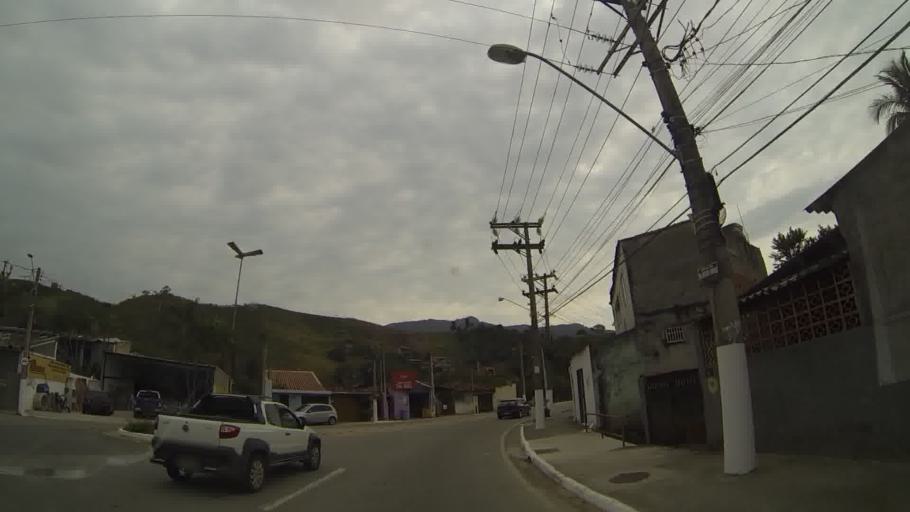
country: BR
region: Sao Paulo
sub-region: Sao Sebastiao
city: Sao Sebastiao
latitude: -23.8152
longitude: -45.4094
